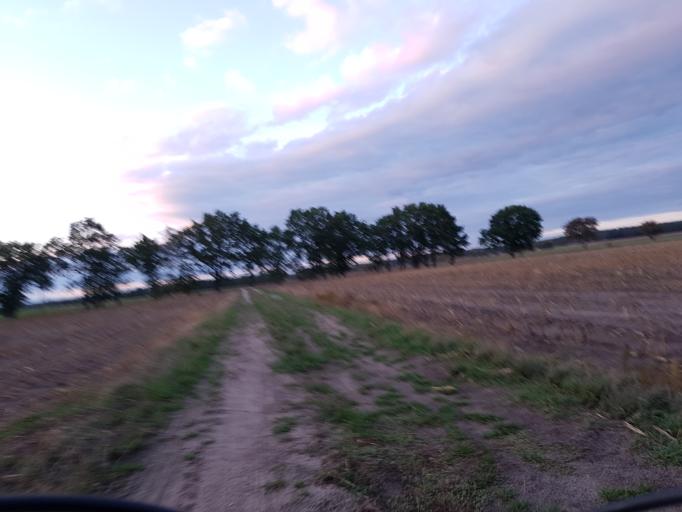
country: DE
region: Brandenburg
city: Schilda
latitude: 51.6070
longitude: 13.3635
